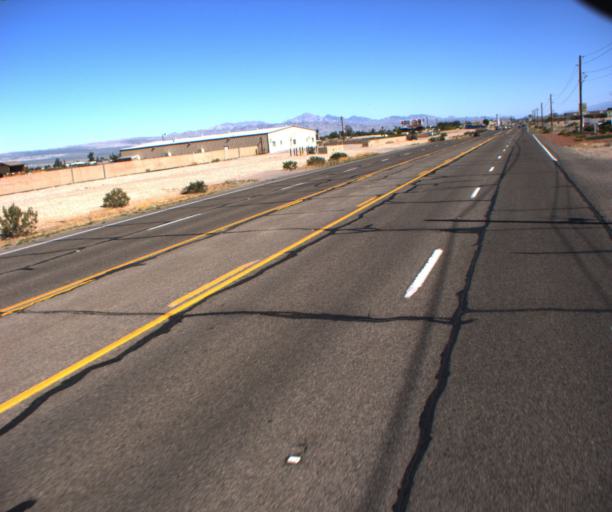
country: US
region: Arizona
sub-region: Mohave County
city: Mohave Valley
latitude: 34.9850
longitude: -114.5979
